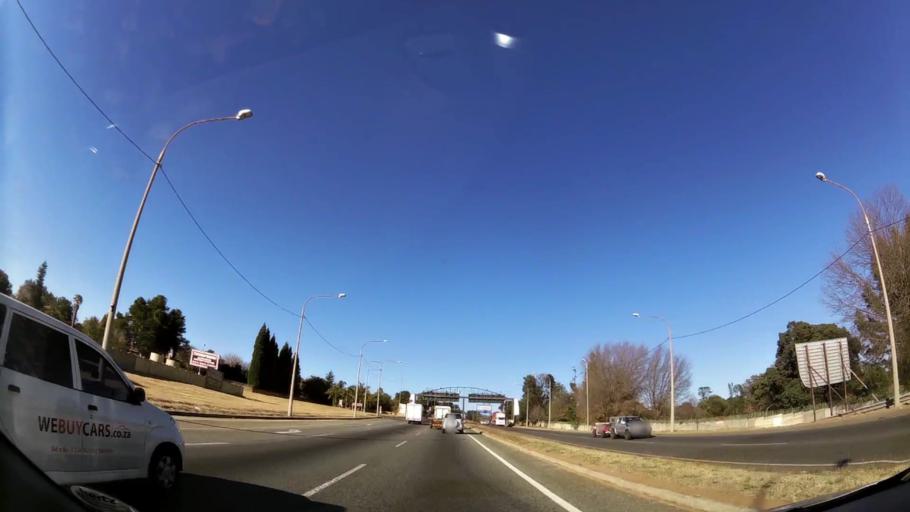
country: ZA
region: Gauteng
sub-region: West Rand District Municipality
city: Krugersdorp
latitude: -26.0814
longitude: 27.7898
